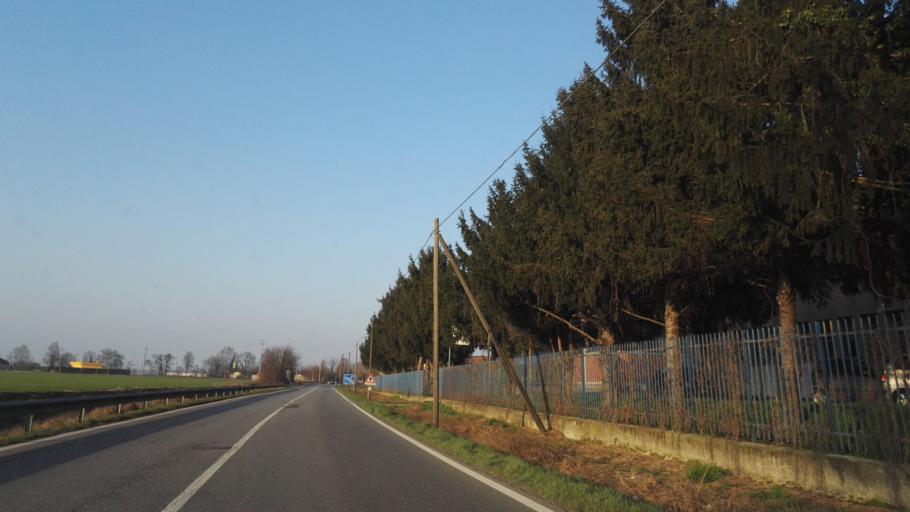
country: IT
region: Lombardy
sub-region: Citta metropolitana di Milano
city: Mombretto
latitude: 45.4083
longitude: 9.3581
